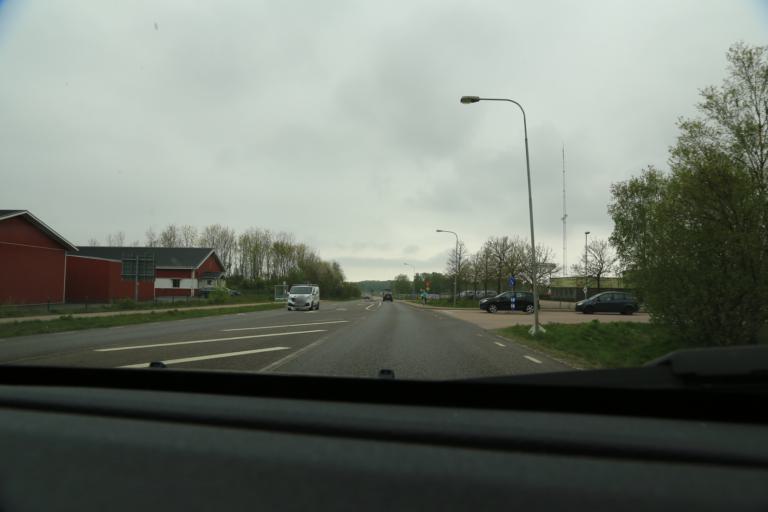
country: SE
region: Halland
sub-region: Kungsbacka Kommun
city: Frillesas
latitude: 57.2405
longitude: 12.1891
